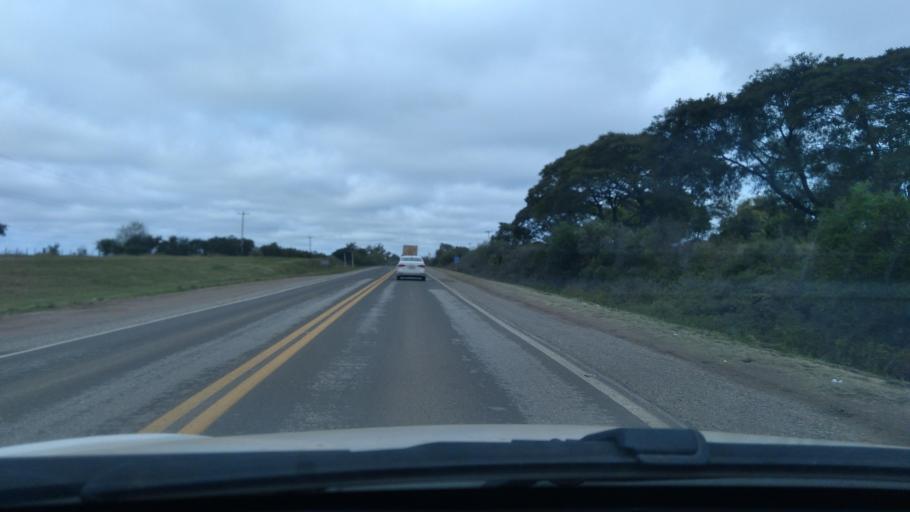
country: BR
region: Rio Grande do Sul
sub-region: Dom Pedrito
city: Dom Pedrito
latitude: -30.9785
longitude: -54.6445
